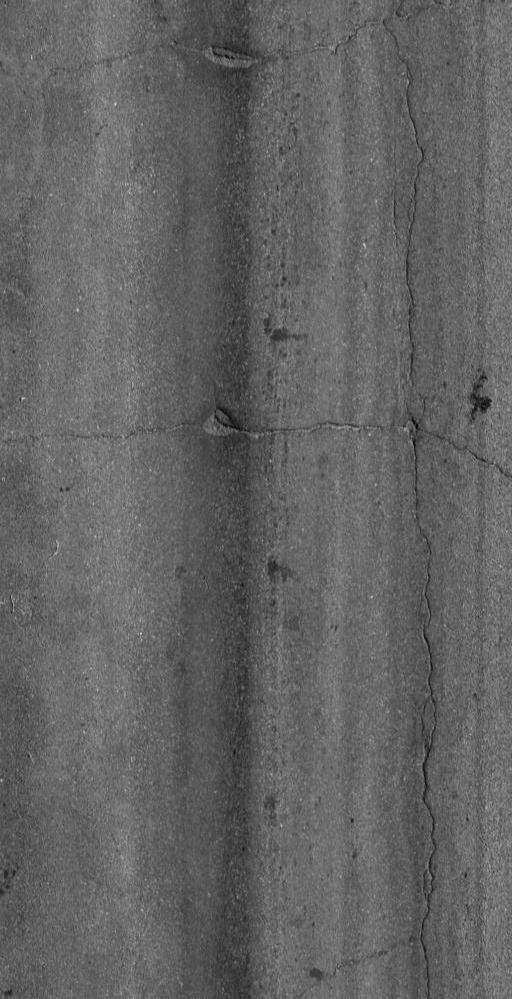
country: US
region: Vermont
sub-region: Chittenden County
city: Burlington
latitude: 44.4895
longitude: -73.2087
